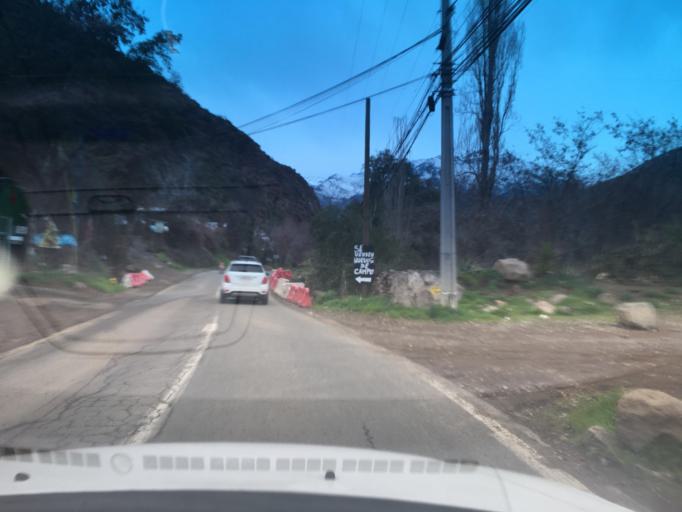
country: CL
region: Santiago Metropolitan
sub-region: Provincia de Cordillera
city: Puente Alto
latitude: -33.6652
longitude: -70.3501
